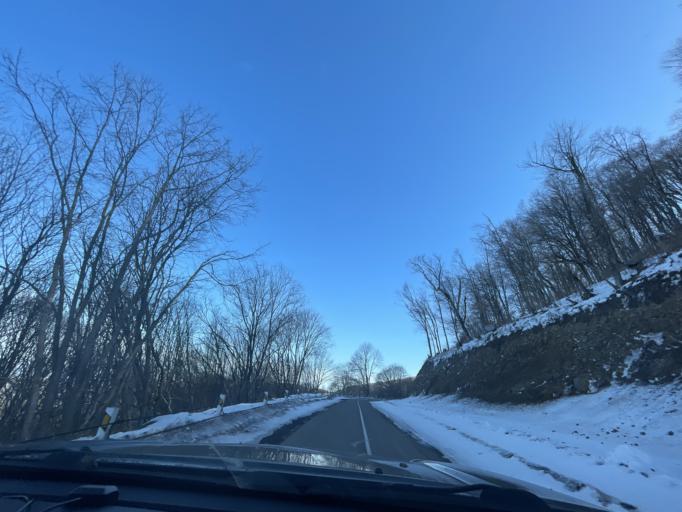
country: GE
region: Kvemo Kartli
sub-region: Tetri Tsqaro
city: Manglisi
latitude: 41.7705
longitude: 44.5067
